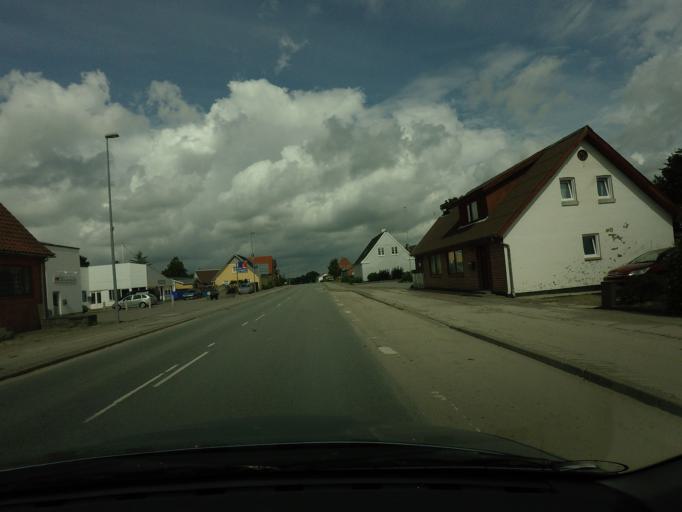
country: DK
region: North Denmark
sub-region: Hjorring Kommune
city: Tars
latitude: 57.3884
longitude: 10.1087
